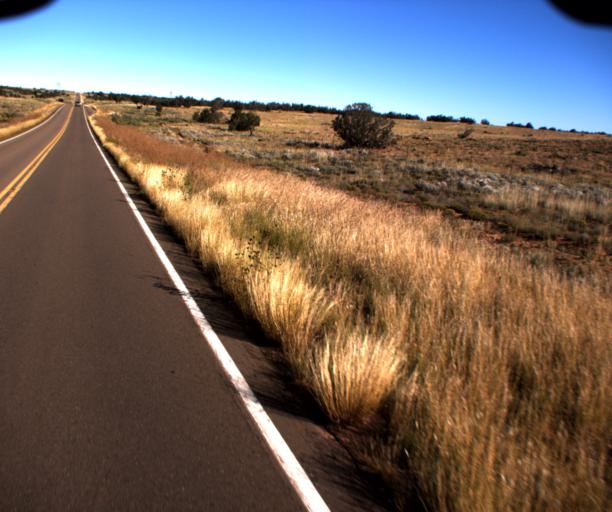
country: US
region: Arizona
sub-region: Navajo County
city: Snowflake
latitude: 34.6071
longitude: -110.0895
